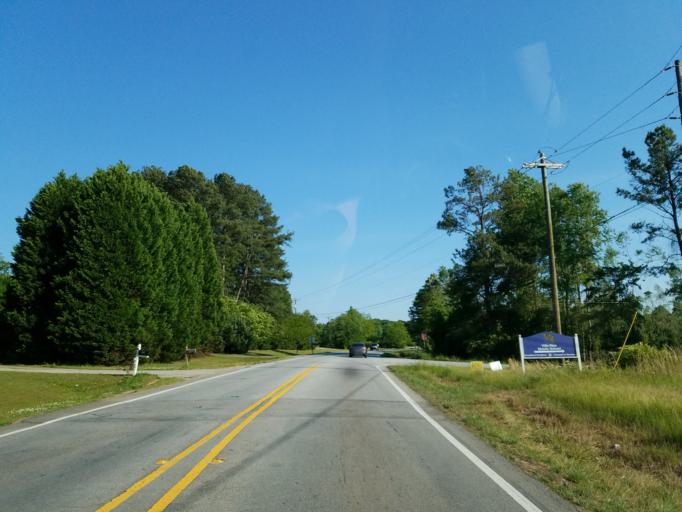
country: US
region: Georgia
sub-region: Carroll County
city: Villa Rica
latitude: 33.7789
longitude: -84.9650
